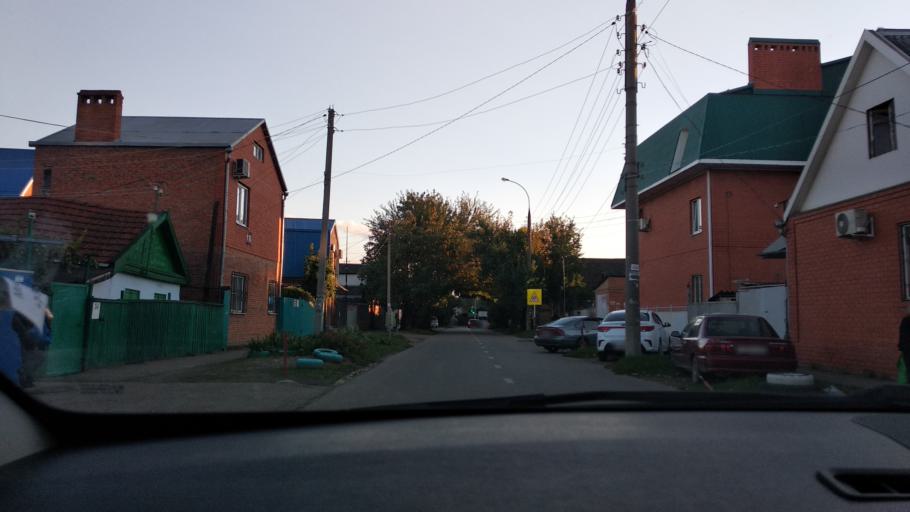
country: RU
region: Krasnodarskiy
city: Krasnodar
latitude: 45.0169
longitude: 38.9983
